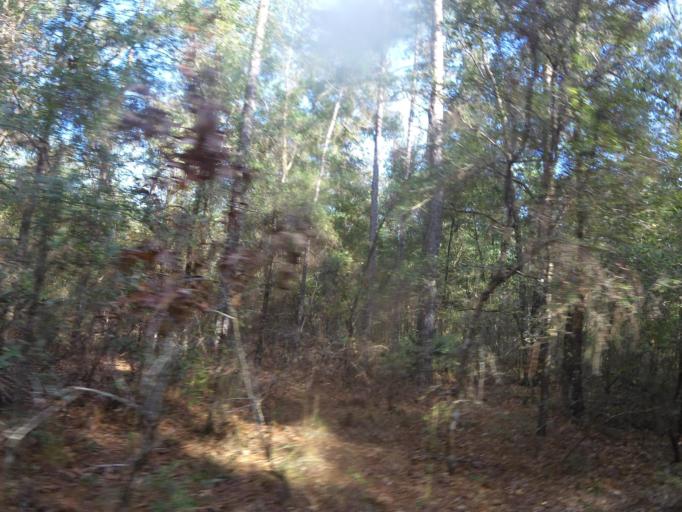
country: US
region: Florida
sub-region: Clay County
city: Middleburg
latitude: 30.1336
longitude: -81.9415
